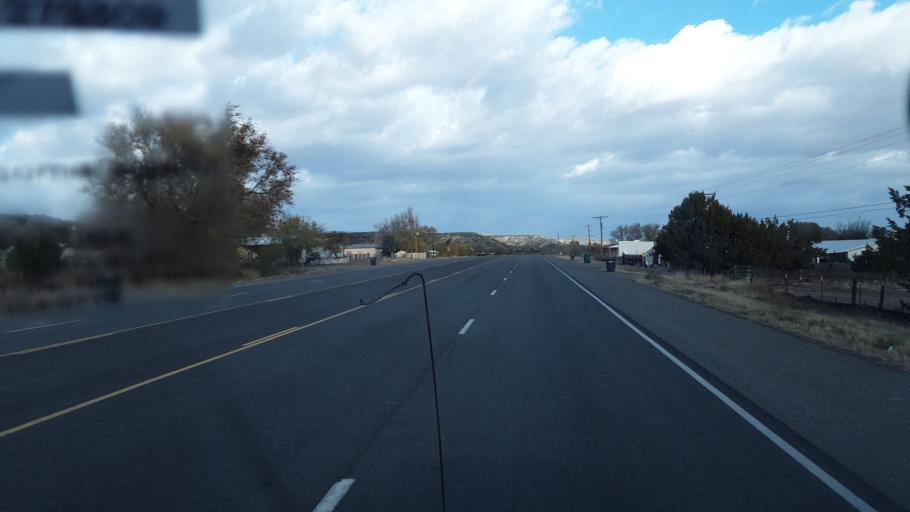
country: US
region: New Mexico
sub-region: Rio Arriba County
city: Ohkay Owingeh
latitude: 36.0436
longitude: -106.1044
